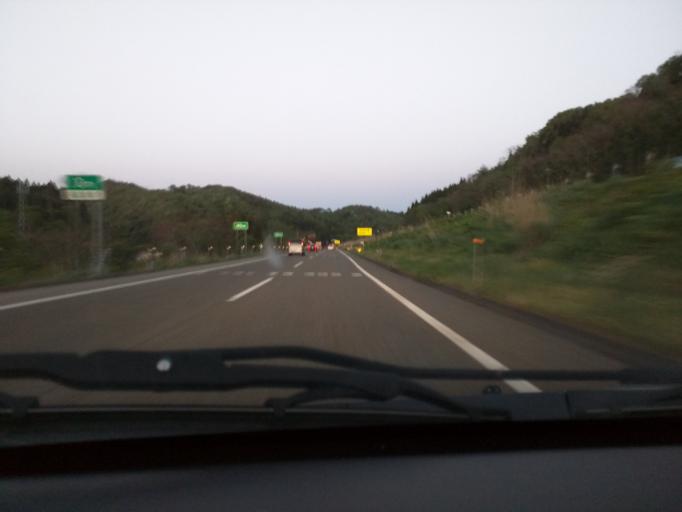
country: JP
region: Niigata
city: Kashiwazaki
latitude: 37.3393
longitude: 138.5311
